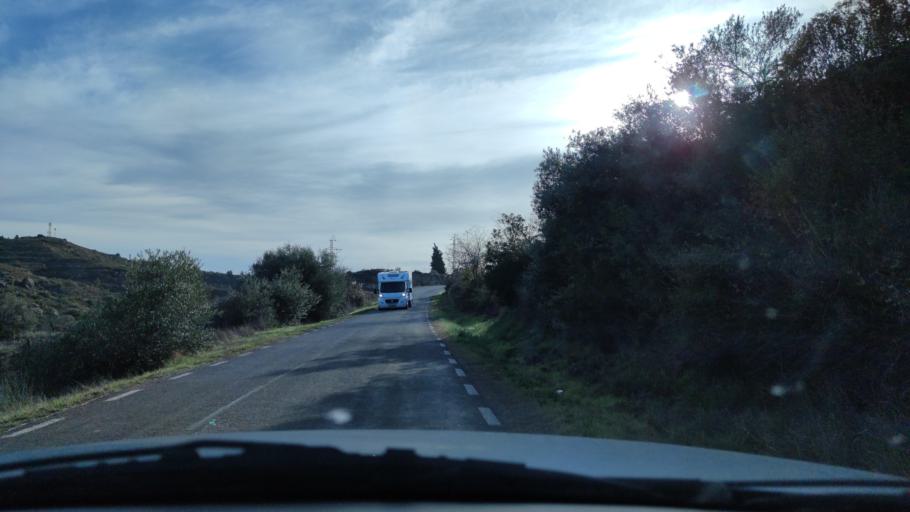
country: ES
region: Catalonia
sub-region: Provincia de Lleida
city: el Cogul
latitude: 41.4704
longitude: 0.6869
